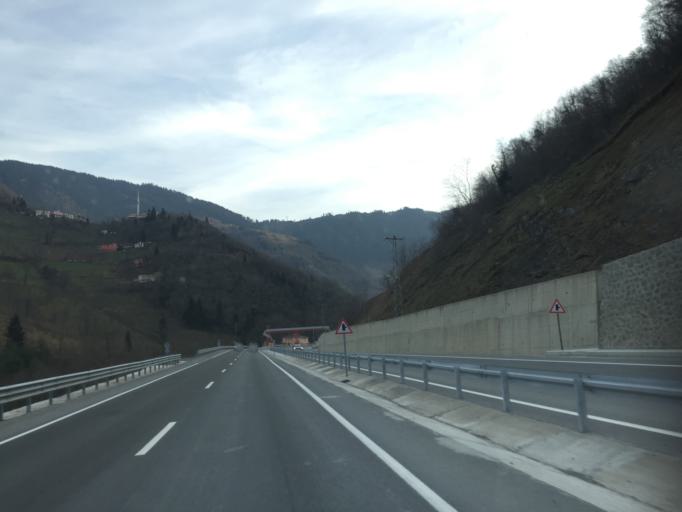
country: TR
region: Trabzon
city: Macka
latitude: 40.7627
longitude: 39.5629
